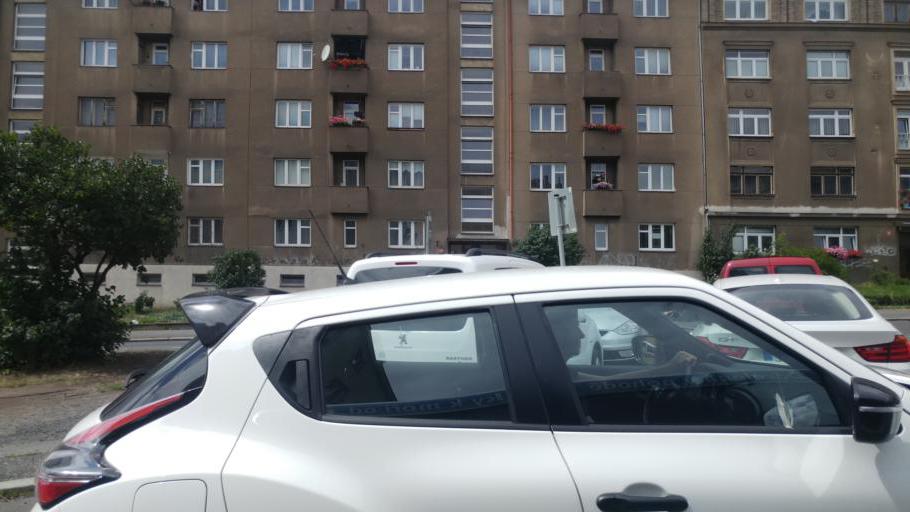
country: CZ
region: Praha
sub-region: Praha 8
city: Karlin
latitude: 50.0705
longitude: 14.4699
